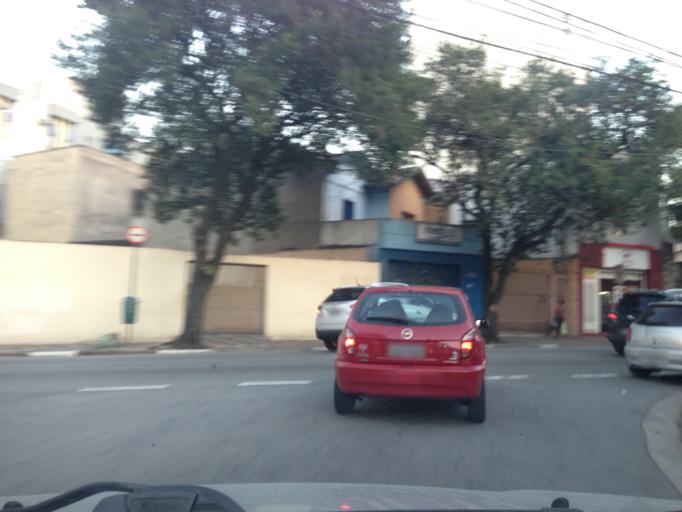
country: BR
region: Sao Paulo
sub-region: Sao Paulo
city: Sao Paulo
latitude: -23.5245
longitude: -46.7058
